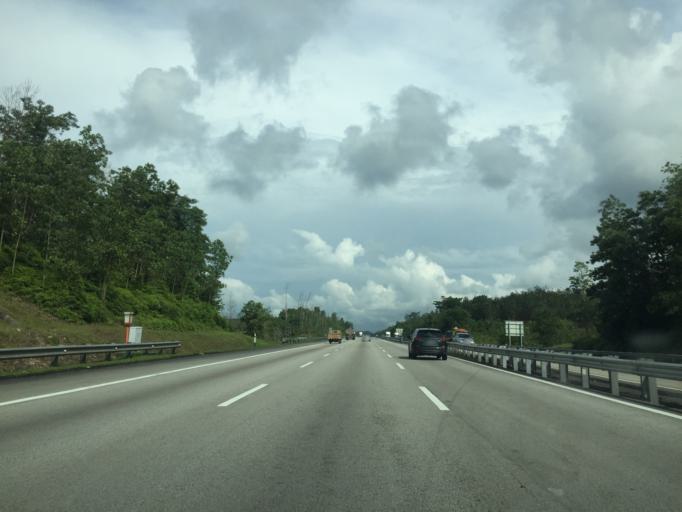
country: MY
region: Selangor
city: Serendah
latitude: 3.5153
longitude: 101.5276
